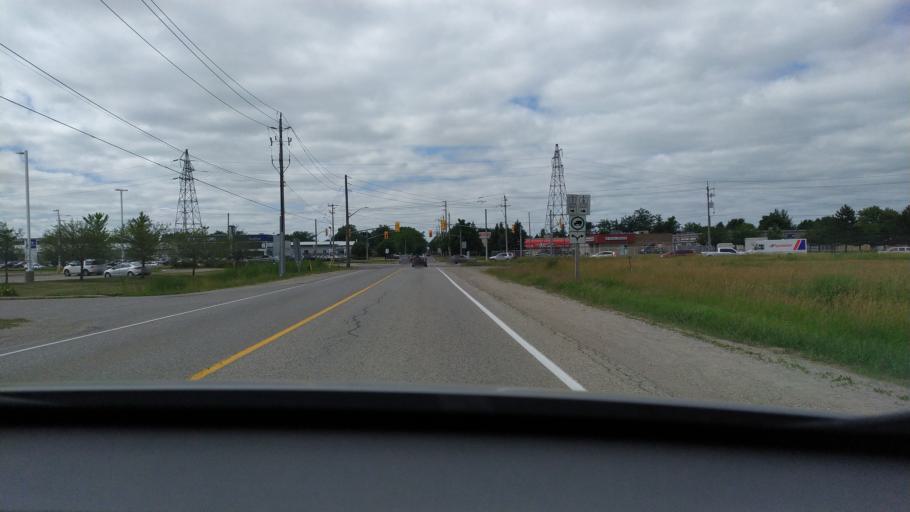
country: CA
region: Ontario
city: Stratford
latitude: 43.3520
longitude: -80.9718
